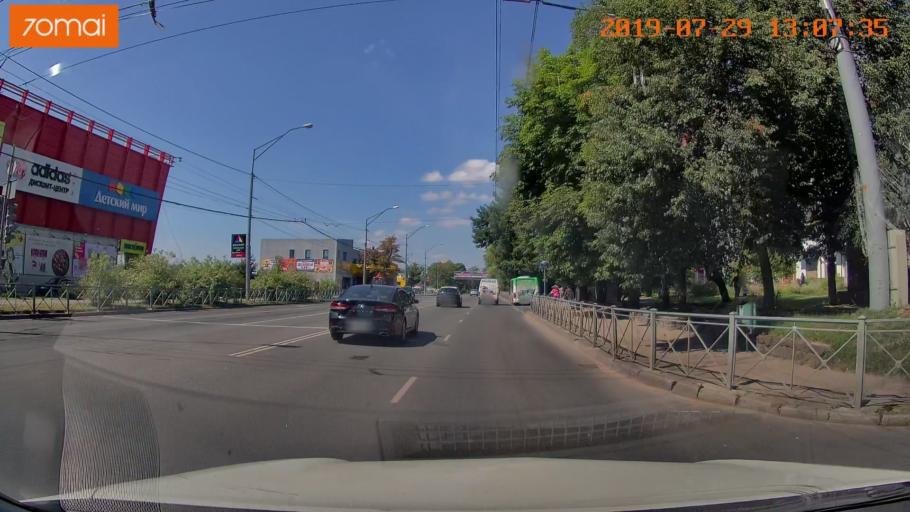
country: RU
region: Kaliningrad
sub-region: Gorod Kaliningrad
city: Kaliningrad
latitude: 54.7105
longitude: 20.4432
